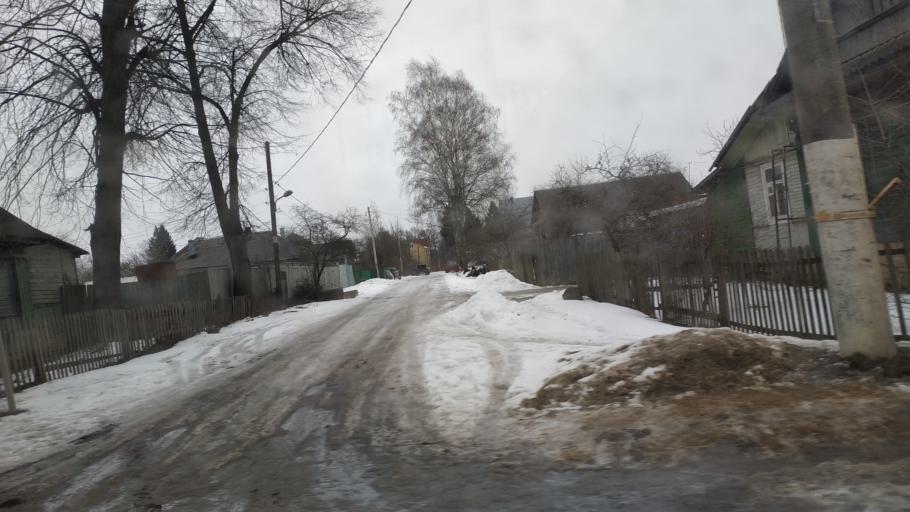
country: RU
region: Tverskaya
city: Tver
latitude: 56.8803
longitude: 35.8996
